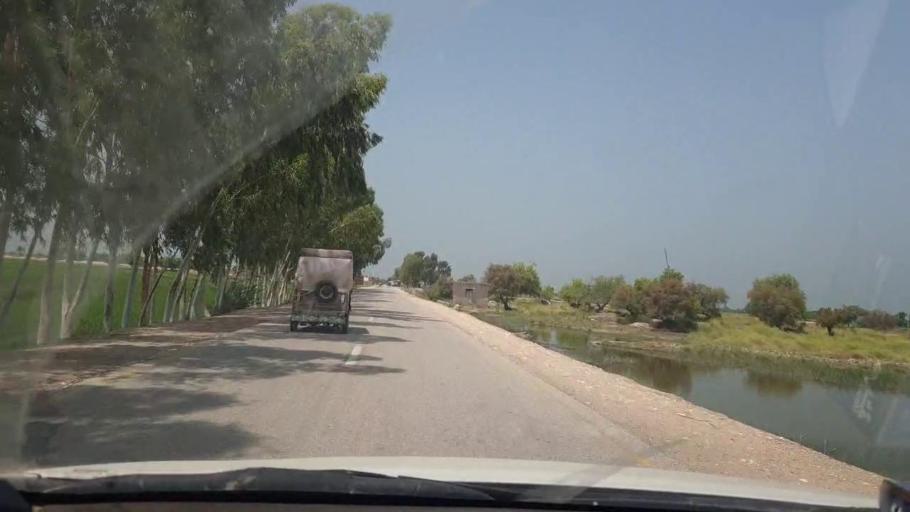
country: PK
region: Sindh
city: Rustam jo Goth
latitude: 27.9553
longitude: 68.7296
